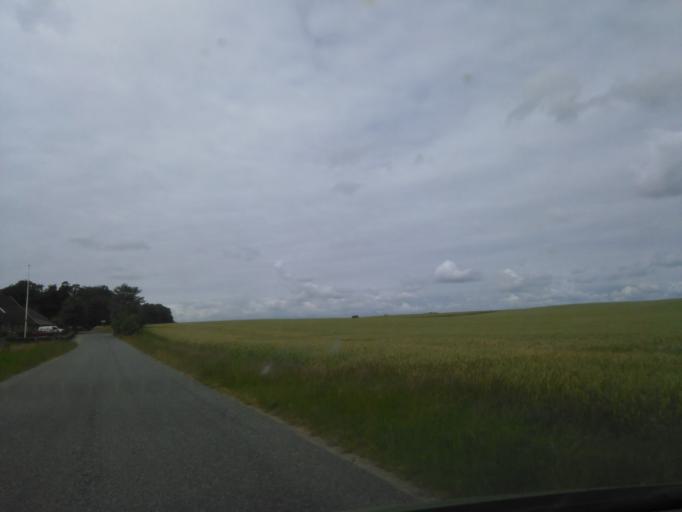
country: DK
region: Central Jutland
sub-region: Arhus Kommune
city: Solbjerg
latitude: 56.0094
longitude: 10.0603
